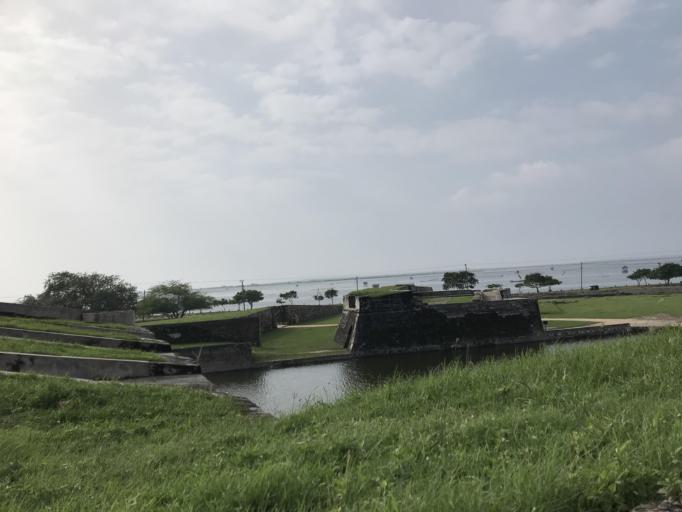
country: LK
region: Northern Province
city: Jaffna
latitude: 9.6613
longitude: 80.0092
